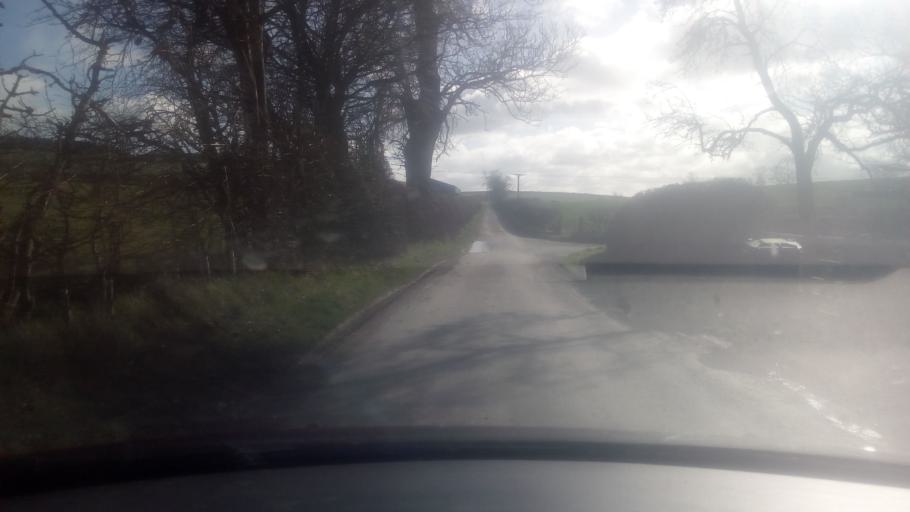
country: GB
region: Scotland
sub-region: The Scottish Borders
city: Saint Boswells
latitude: 55.5320
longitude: -2.6424
